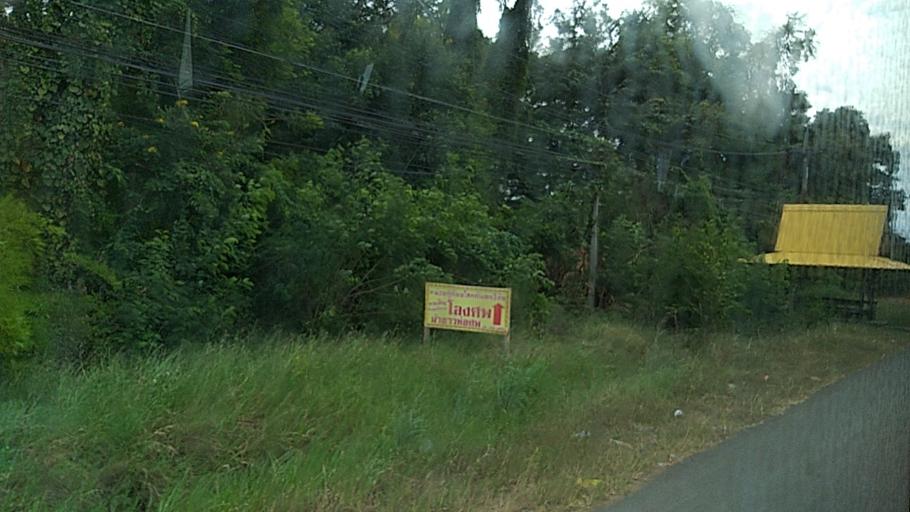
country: TH
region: Maha Sarakham
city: Kantharawichai
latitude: 16.3080
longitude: 103.3001
